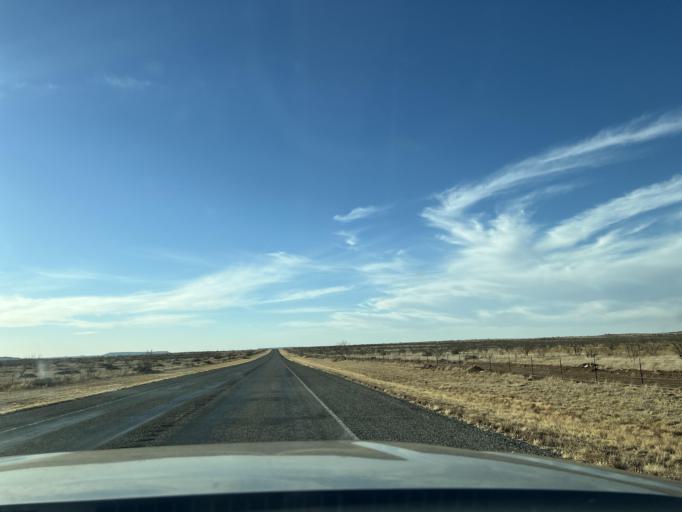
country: US
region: Texas
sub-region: Borden County
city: Gail
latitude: 32.7624
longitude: -101.2723
